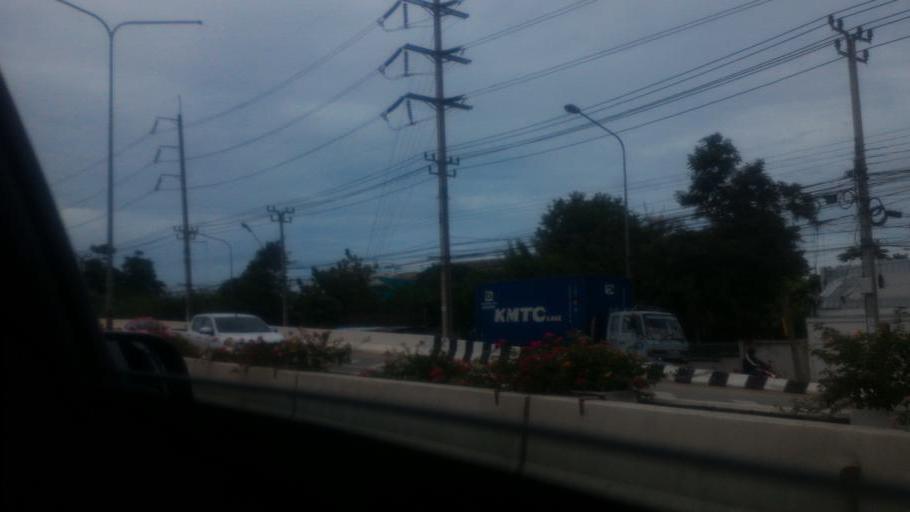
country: TH
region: Bangkok
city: Bang Khun Thian
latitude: 13.6255
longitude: 100.4352
